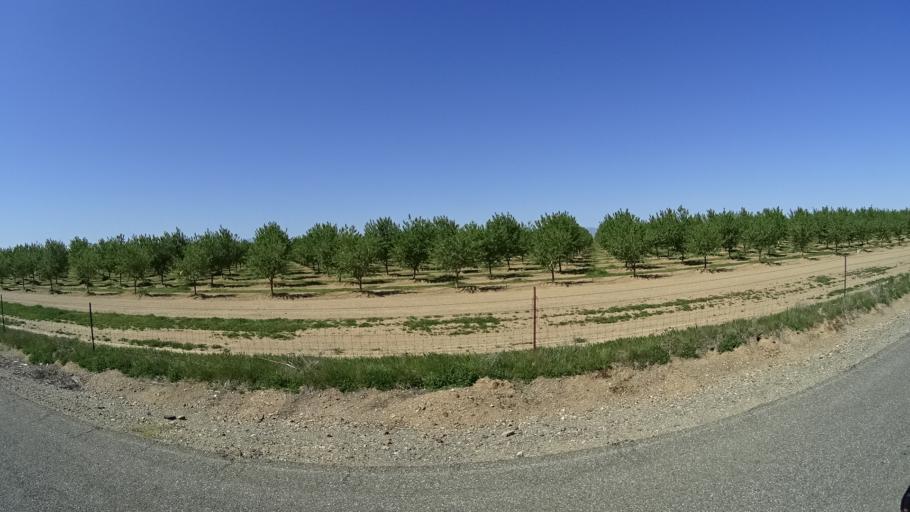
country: US
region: California
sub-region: Glenn County
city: Orland
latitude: 39.6562
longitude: -122.2532
